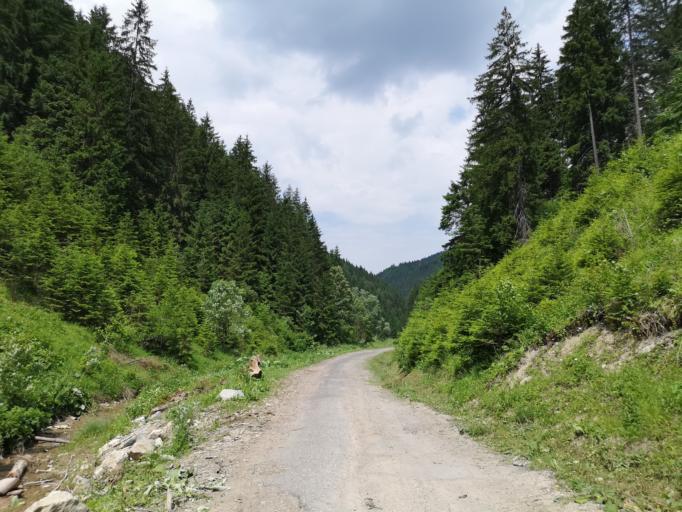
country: SK
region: Zilinsky
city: Ruzomberok
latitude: 49.1395
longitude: 19.4188
